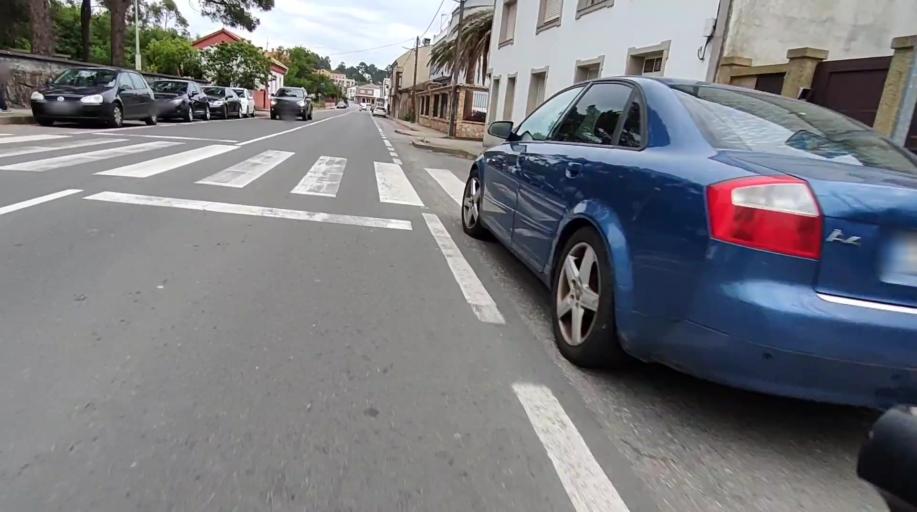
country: ES
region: Galicia
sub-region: Provincia da Coruna
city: Boiro
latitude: 42.6377
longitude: -8.8776
